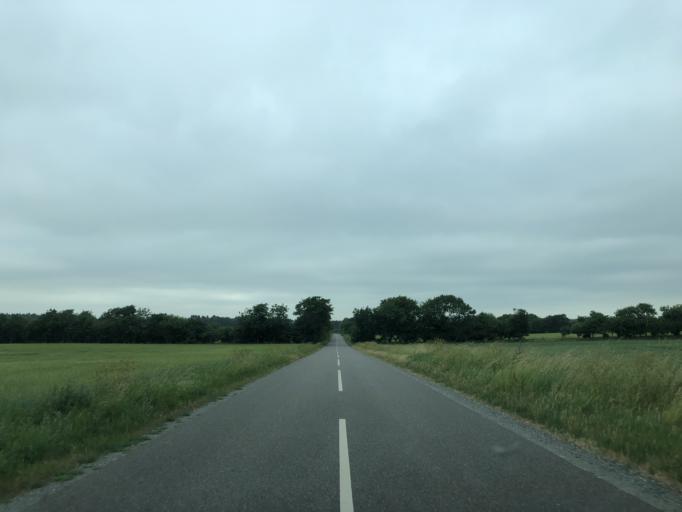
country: DK
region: Central Jutland
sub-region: Holstebro Kommune
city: Holstebro
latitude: 56.2439
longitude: 8.6226
